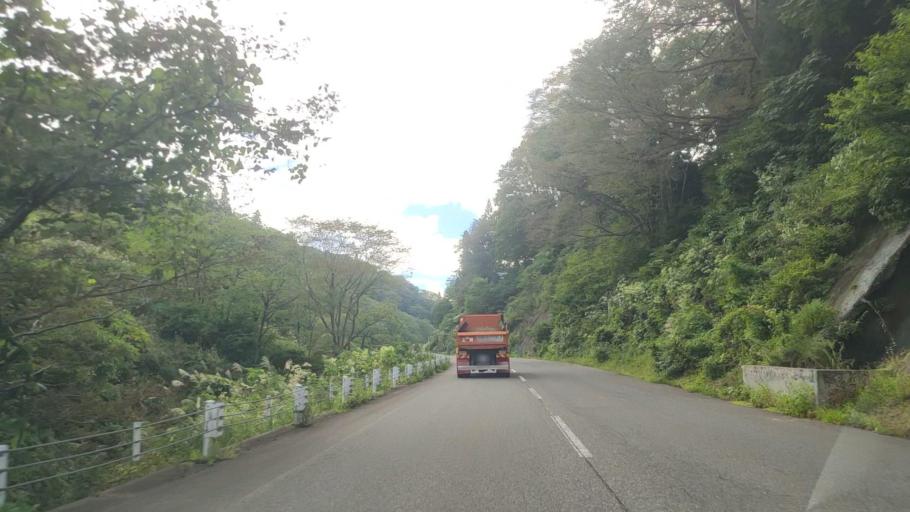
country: JP
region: Nagano
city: Iiyama
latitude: 36.8985
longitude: 138.3194
